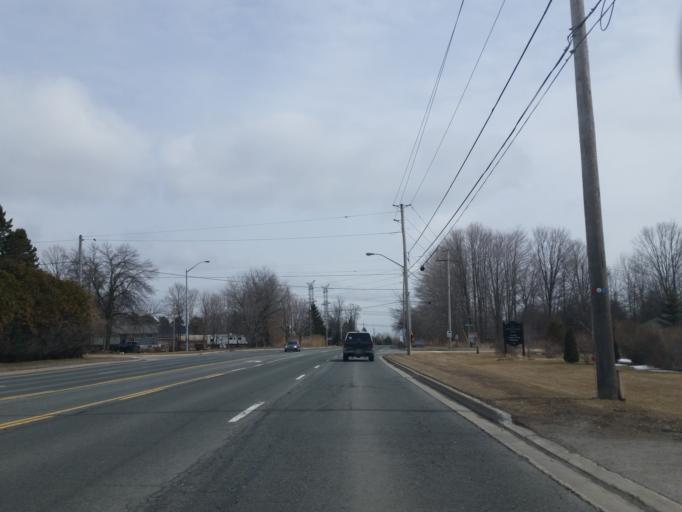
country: CA
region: Ontario
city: Oshawa
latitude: 43.9139
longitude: -78.7473
